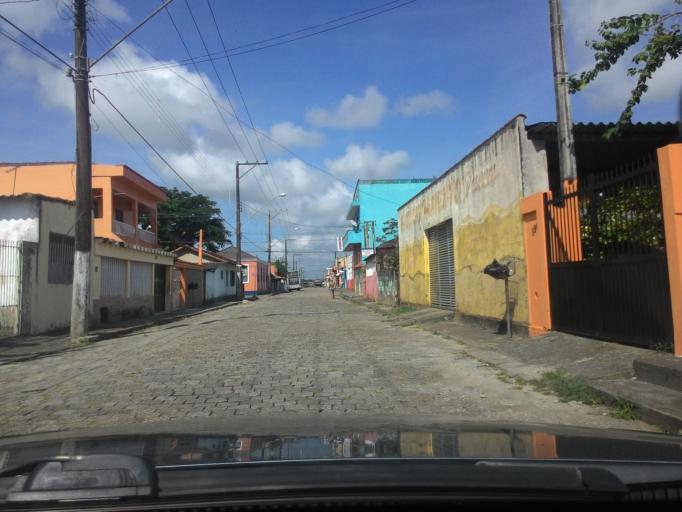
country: BR
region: Sao Paulo
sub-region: Iguape
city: Iguape
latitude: -24.7085
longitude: -47.5601
